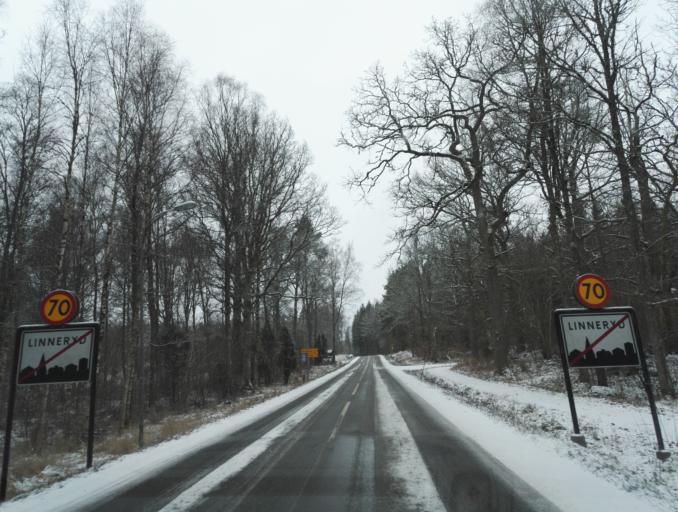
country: SE
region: Kronoberg
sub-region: Lessebo Kommun
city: Hovmantorp
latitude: 56.6525
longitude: 15.1293
